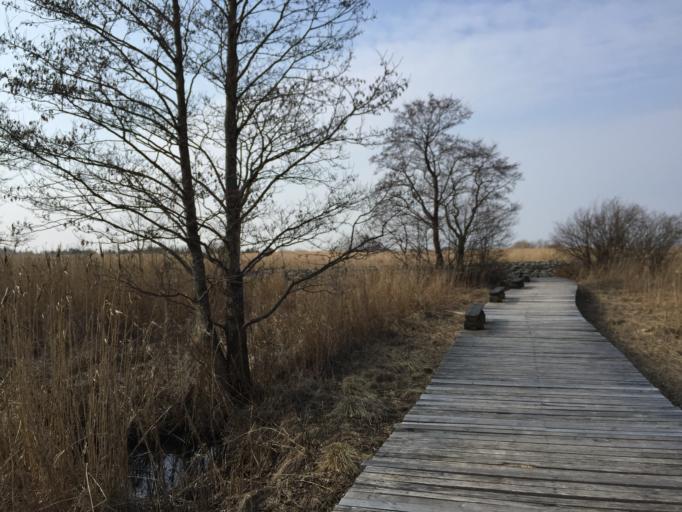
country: LV
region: Salacgrivas
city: Ainazi
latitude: 57.8735
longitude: 24.3584
